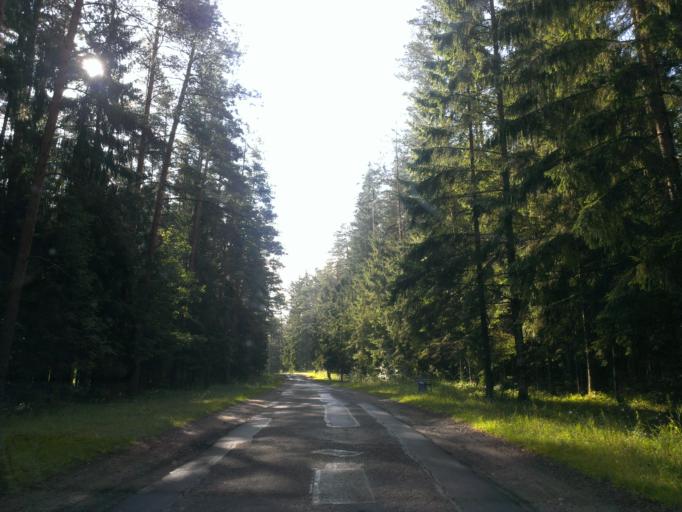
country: LV
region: Incukalns
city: Vangazi
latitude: 57.0966
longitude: 24.5359
